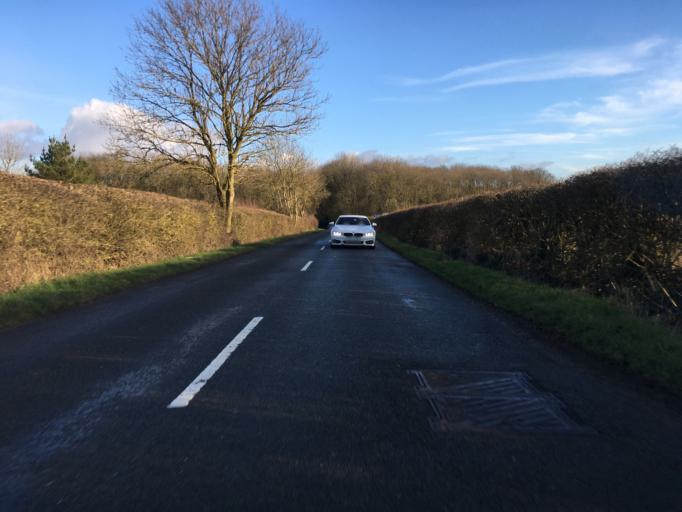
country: GB
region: England
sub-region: Warwickshire
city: Stratford-upon-Avon
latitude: 52.2410
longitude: -1.7171
